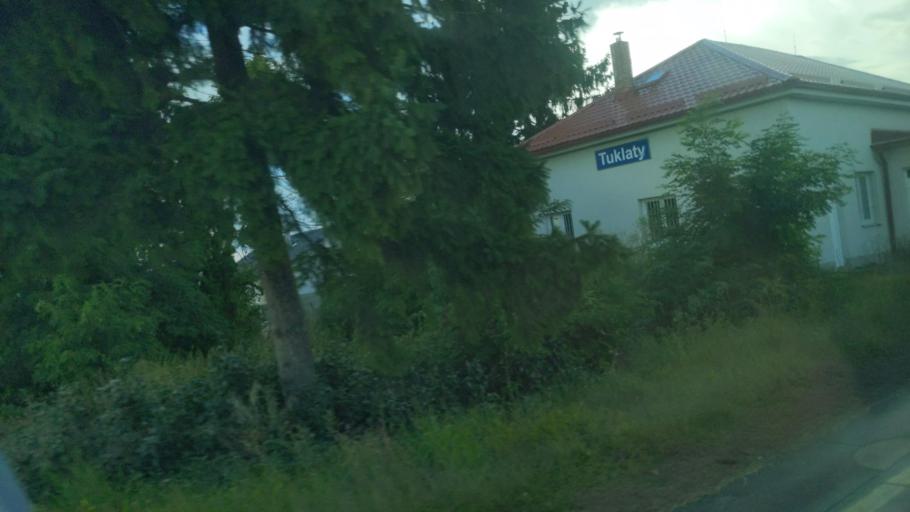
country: CZ
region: Central Bohemia
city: Uvaly
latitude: 50.0770
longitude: 14.7699
